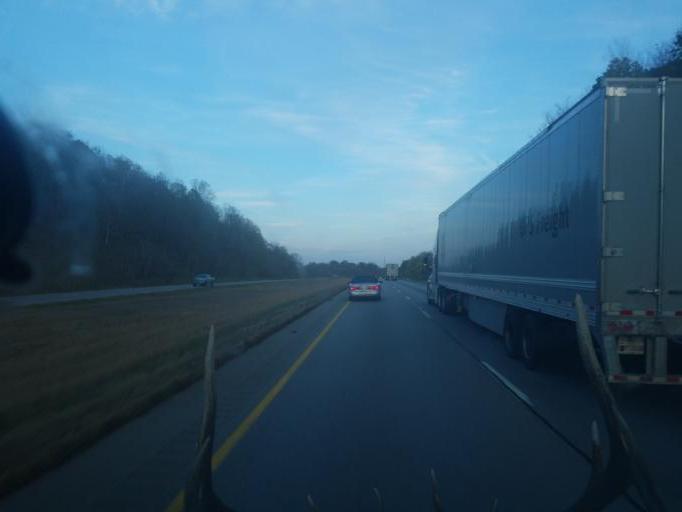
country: US
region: Ohio
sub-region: Muskingum County
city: New Concord
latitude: 39.9776
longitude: -81.7758
